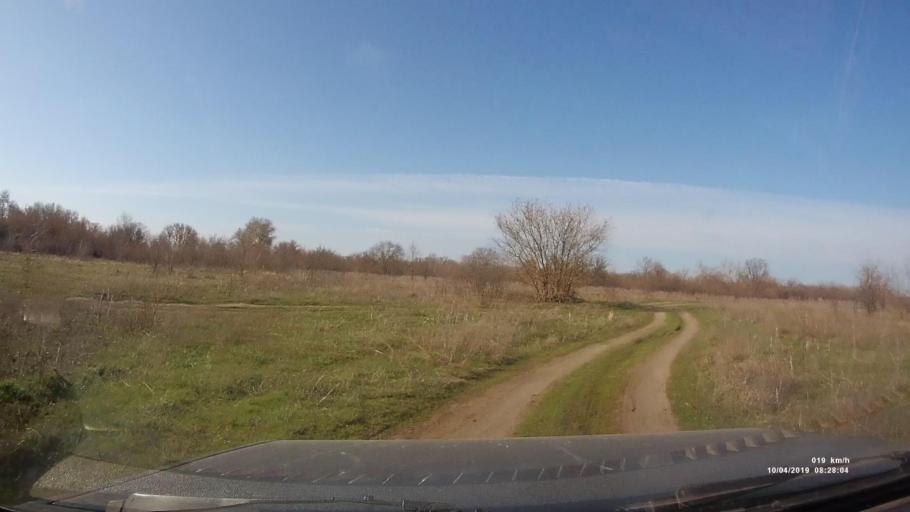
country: RU
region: Rostov
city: Kamensk-Shakhtinskiy
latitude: 48.3569
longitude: 40.2243
